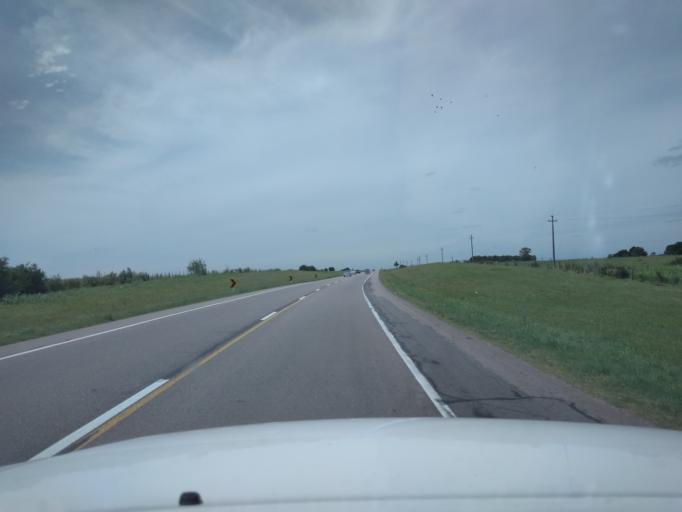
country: UY
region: Florida
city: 25 de Mayo
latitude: -34.2314
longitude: -56.2129
